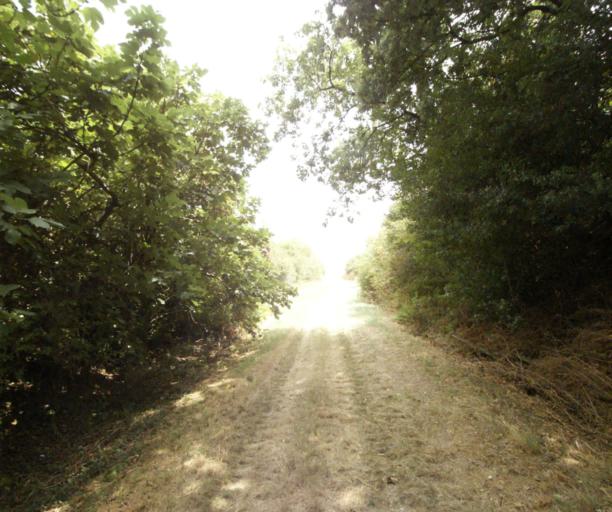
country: FR
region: Midi-Pyrenees
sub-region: Departement de la Haute-Garonne
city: Saint-Felix-Lauragais
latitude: 43.4400
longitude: 1.8926
